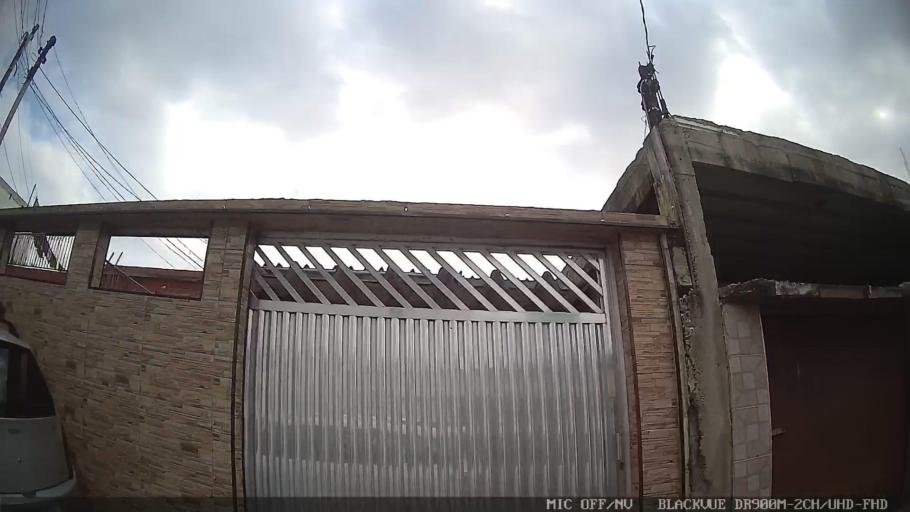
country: BR
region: Sao Paulo
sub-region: Santos
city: Santos
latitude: -23.9498
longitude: -46.2841
